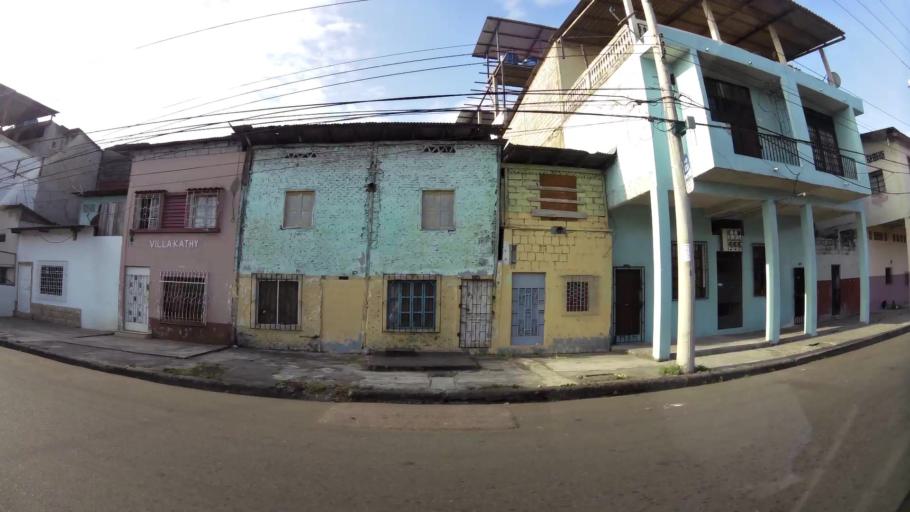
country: EC
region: Guayas
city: Guayaquil
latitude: -2.2106
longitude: -79.9013
